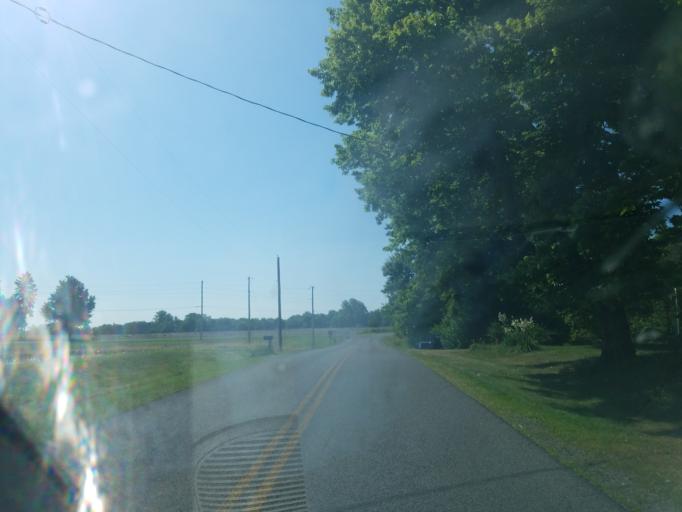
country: US
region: Ohio
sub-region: Logan County
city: Northwood
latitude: 40.4262
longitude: -83.7052
